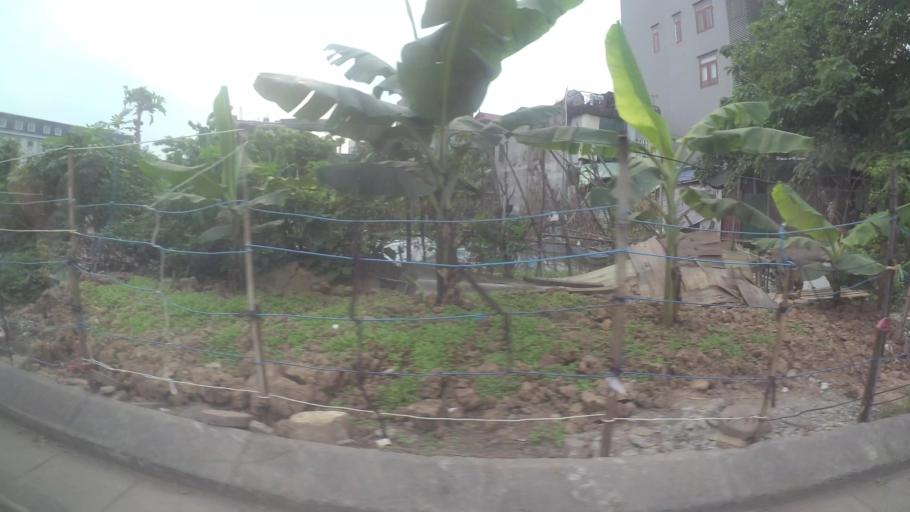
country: VN
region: Ha Noi
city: Cau Dien
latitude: 21.0427
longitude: 105.7520
